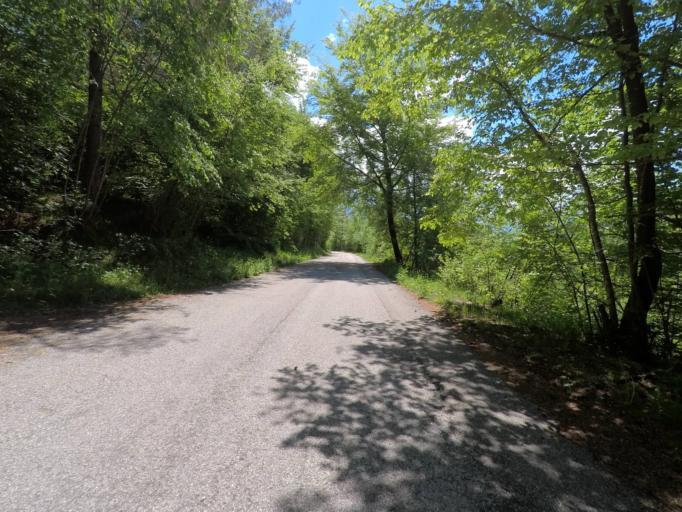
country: IT
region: Friuli Venezia Giulia
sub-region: Provincia di Udine
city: Raveo
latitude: 46.4454
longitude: 12.8791
